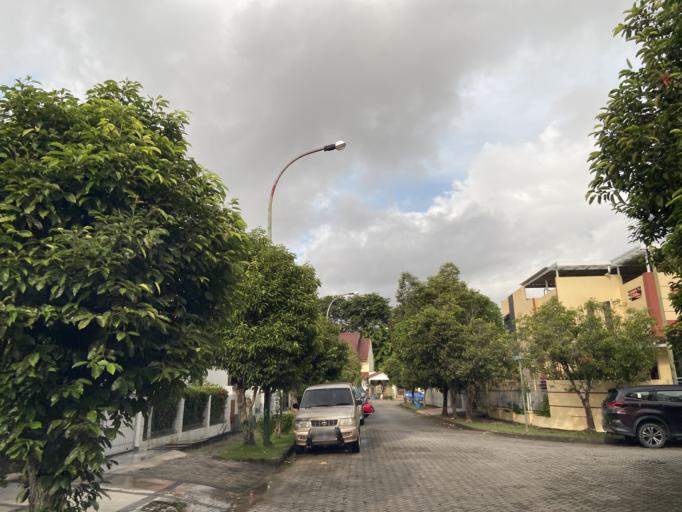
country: SG
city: Singapore
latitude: 1.1086
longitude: 104.0270
